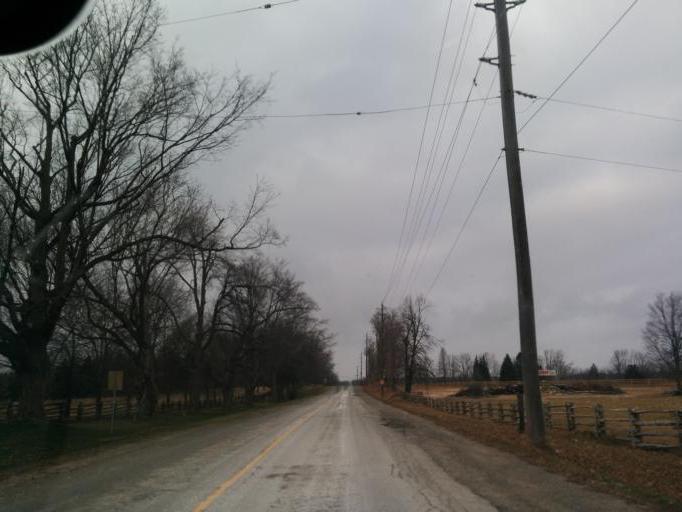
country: CA
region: Ontario
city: Orangeville
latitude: 43.8010
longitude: -79.9397
